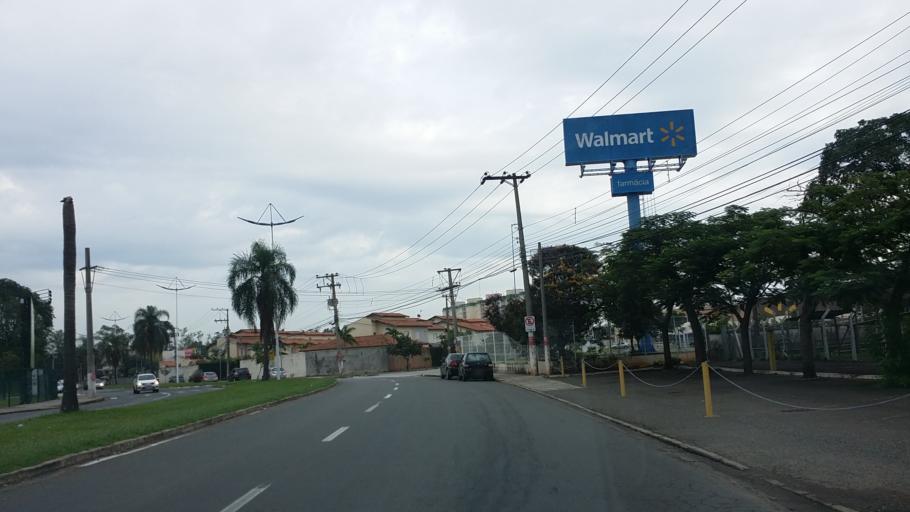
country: BR
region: Sao Paulo
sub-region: Indaiatuba
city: Indaiatuba
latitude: -23.1148
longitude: -47.2182
